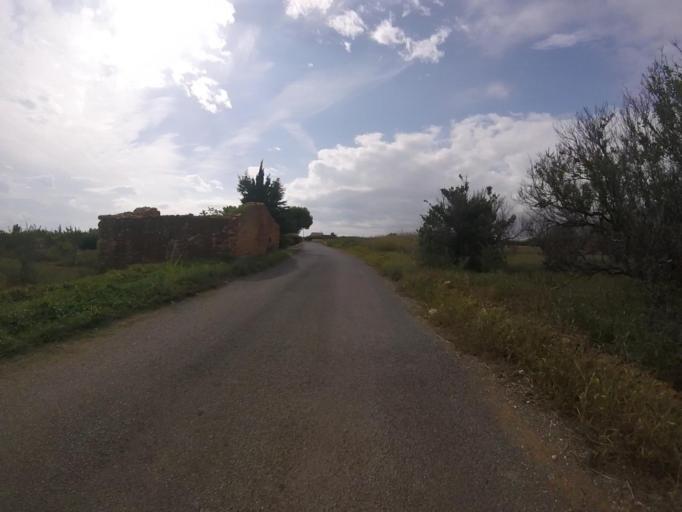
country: ES
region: Valencia
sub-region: Provincia de Castello
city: Torreblanca
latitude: 40.1652
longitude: 0.1698
